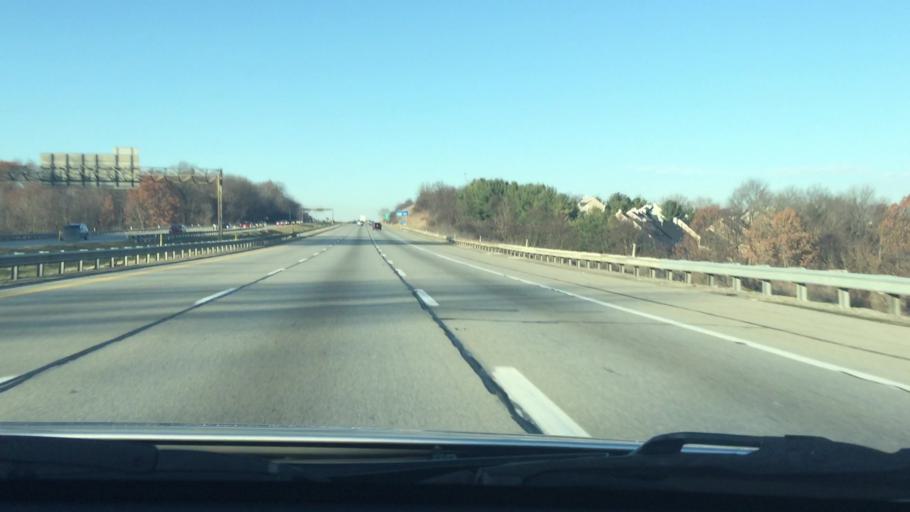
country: US
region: Pennsylvania
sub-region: Allegheny County
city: Franklin Park
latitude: 40.6018
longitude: -80.0936
